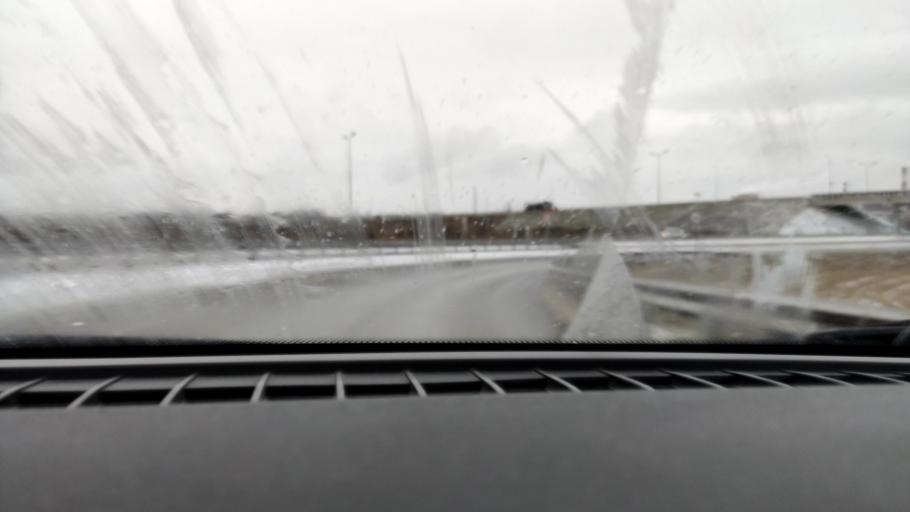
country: RU
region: Perm
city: Kondratovo
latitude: 57.9296
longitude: 56.1758
